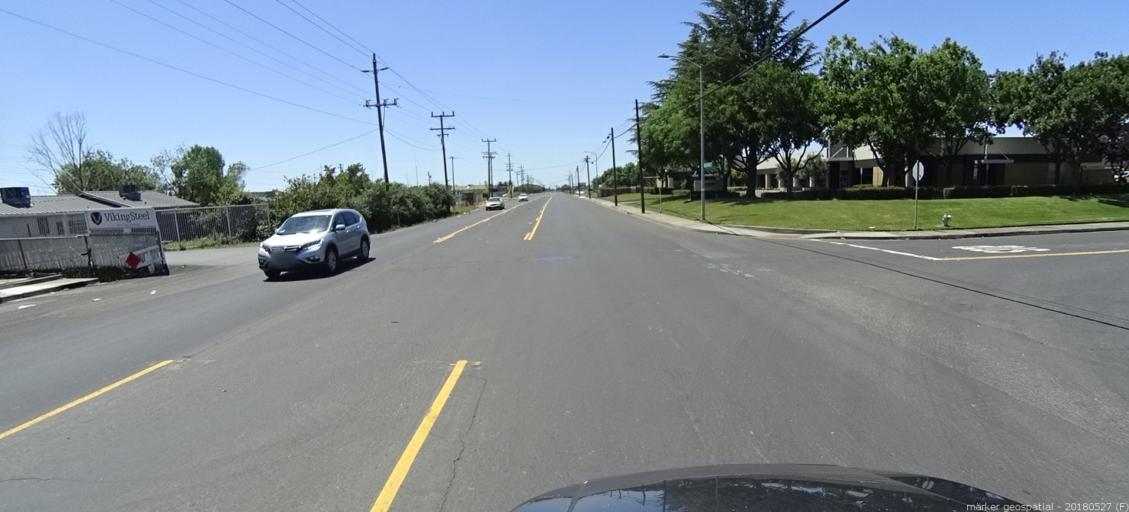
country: US
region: California
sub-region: Sacramento County
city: Florin
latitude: 38.5107
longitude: -121.3845
